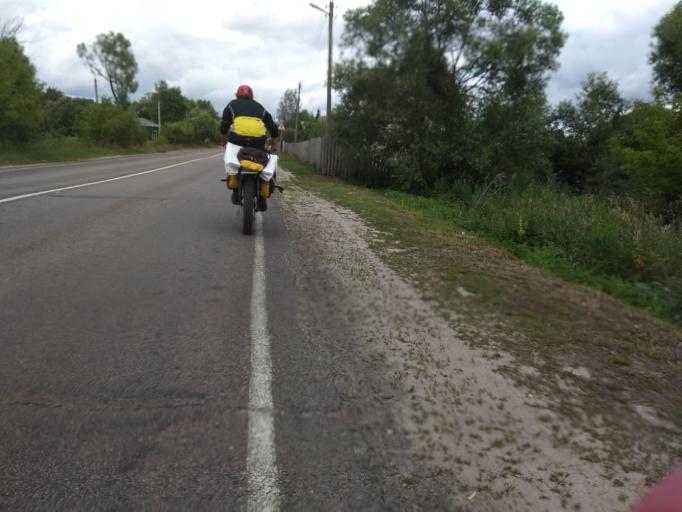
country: RU
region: Moskovskaya
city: Misheronskiy
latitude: 55.6011
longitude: 39.7062
